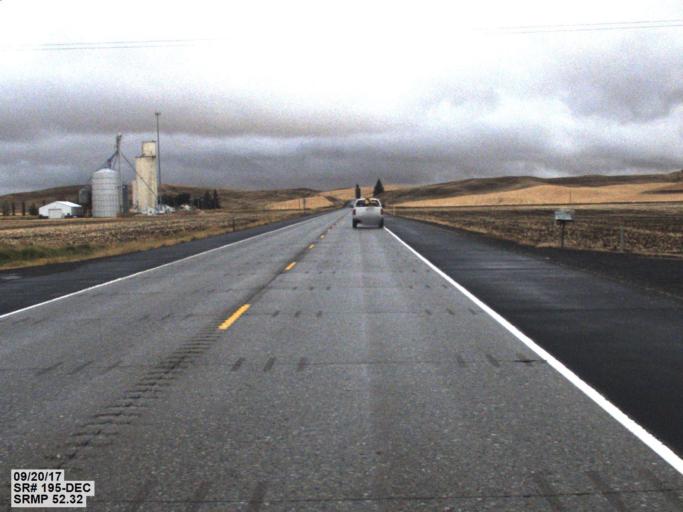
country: US
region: Washington
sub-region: Whitman County
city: Colfax
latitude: 47.0646
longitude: -117.3819
